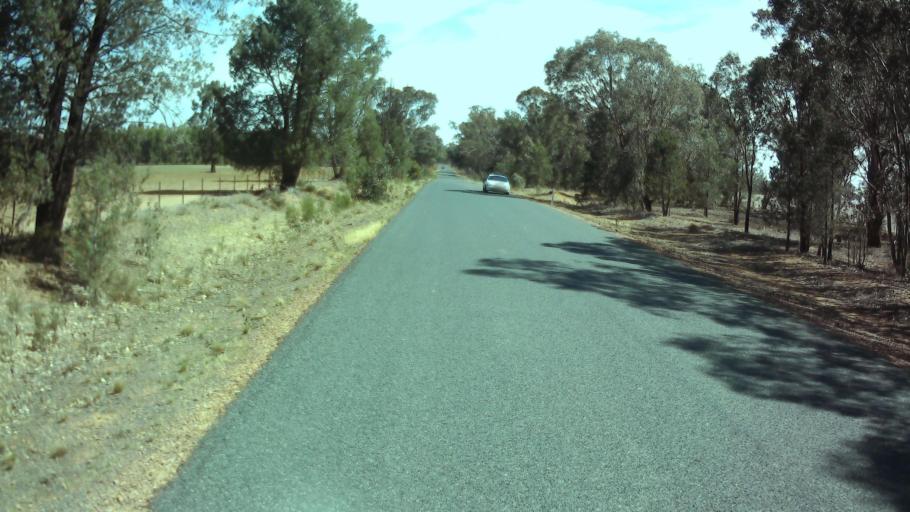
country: AU
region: New South Wales
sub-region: Weddin
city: Grenfell
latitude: -34.0405
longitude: 148.1339
